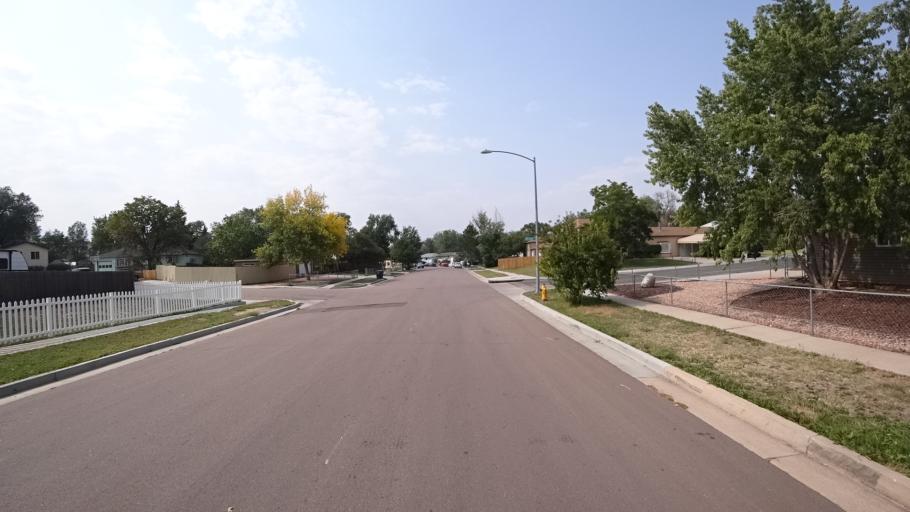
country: US
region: Colorado
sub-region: El Paso County
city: Stratmoor
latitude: 38.8280
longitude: -104.7520
